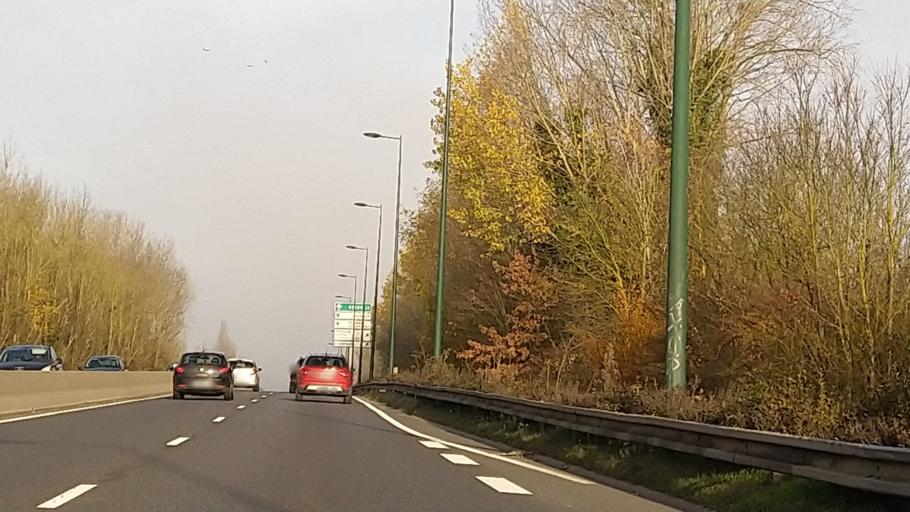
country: FR
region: Ile-de-France
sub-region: Departement du Val-d'Oise
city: Champagne-sur-Oise
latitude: 49.1372
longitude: 2.2544
